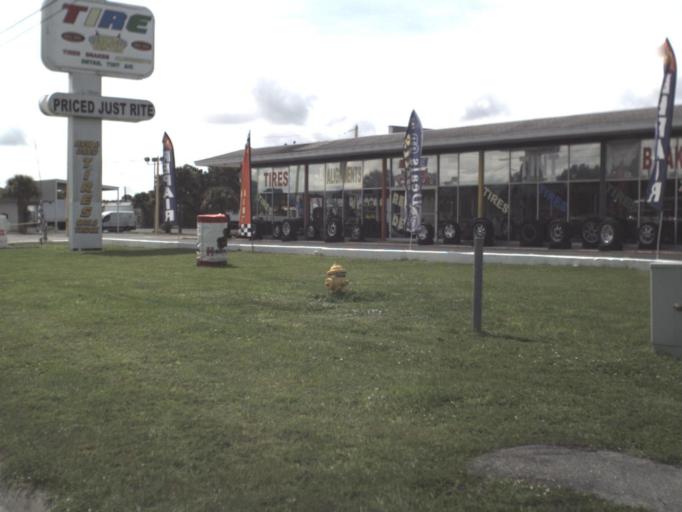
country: US
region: Florida
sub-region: Lee County
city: Fort Myers
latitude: 26.6262
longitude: -81.8621
